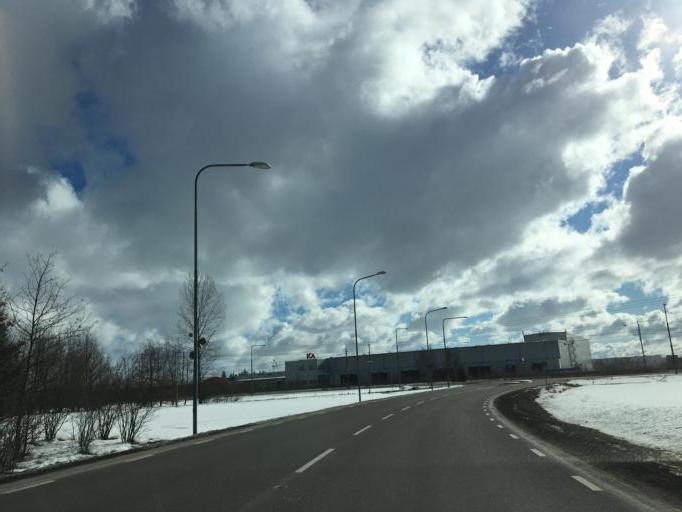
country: SE
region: Vaestmanland
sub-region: Vasteras
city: Vasteras
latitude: 59.5916
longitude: 16.4695
